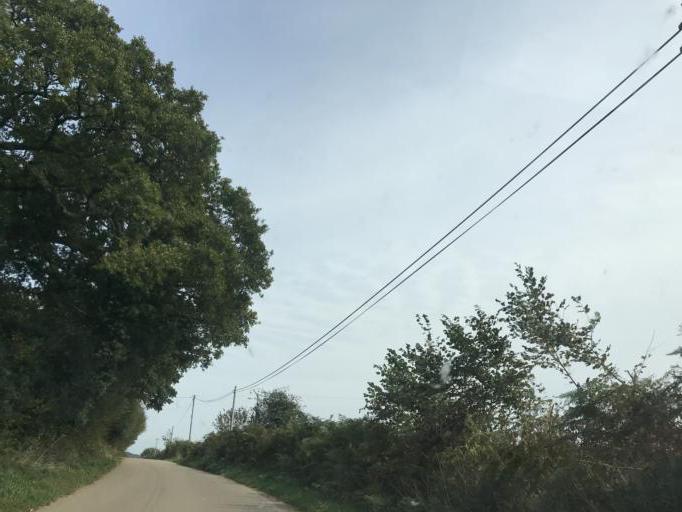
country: FR
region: Brittany
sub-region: Departement du Finistere
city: Brasparts
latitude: 48.3249
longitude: -3.9209
